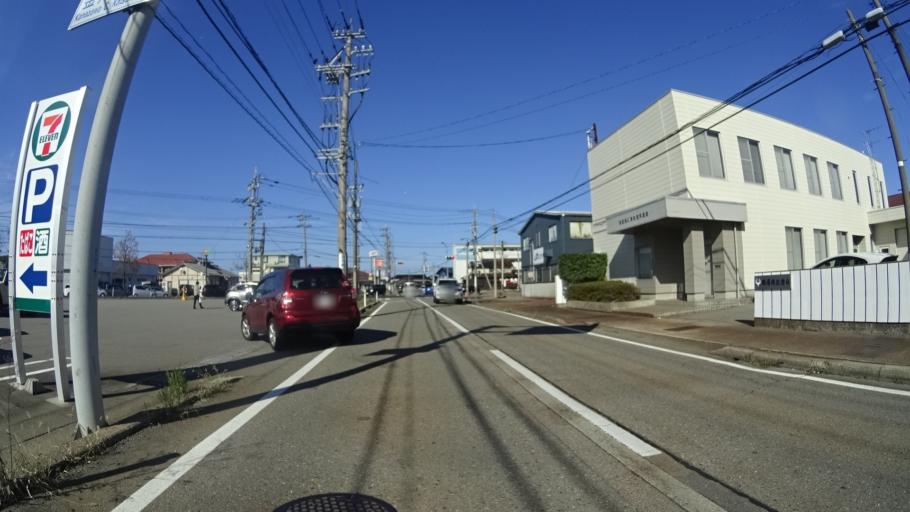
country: JP
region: Ishikawa
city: Kanazawa-shi
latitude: 36.6047
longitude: 136.6071
